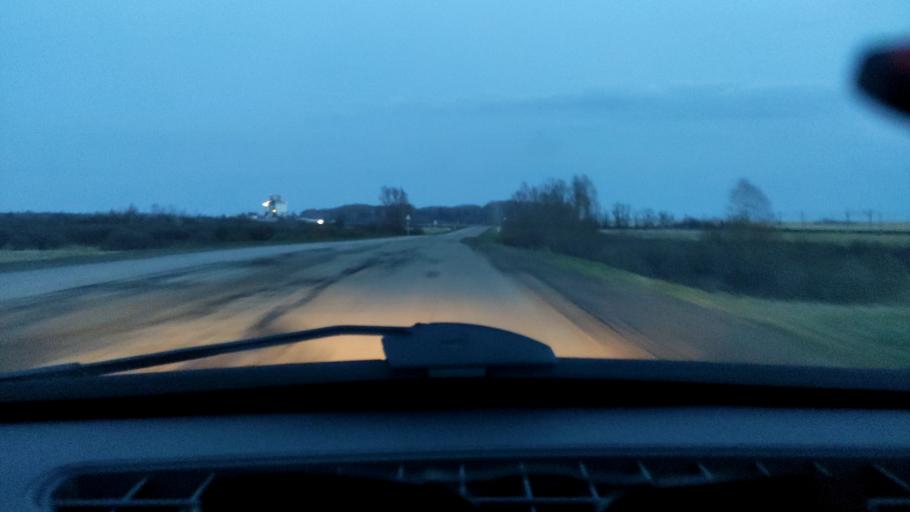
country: RU
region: Bashkortostan
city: Ulukulevo
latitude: 54.4482
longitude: 56.2615
